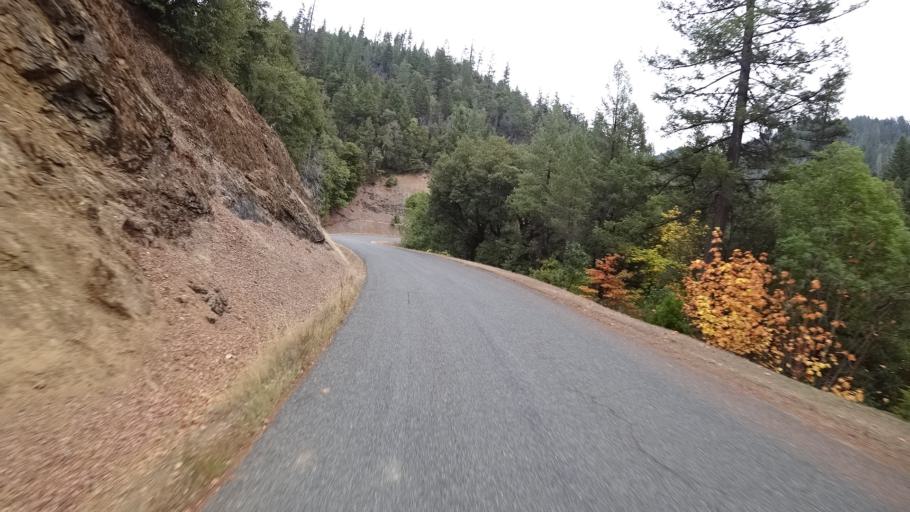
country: US
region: California
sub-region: Siskiyou County
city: Happy Camp
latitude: 41.7581
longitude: -123.3600
